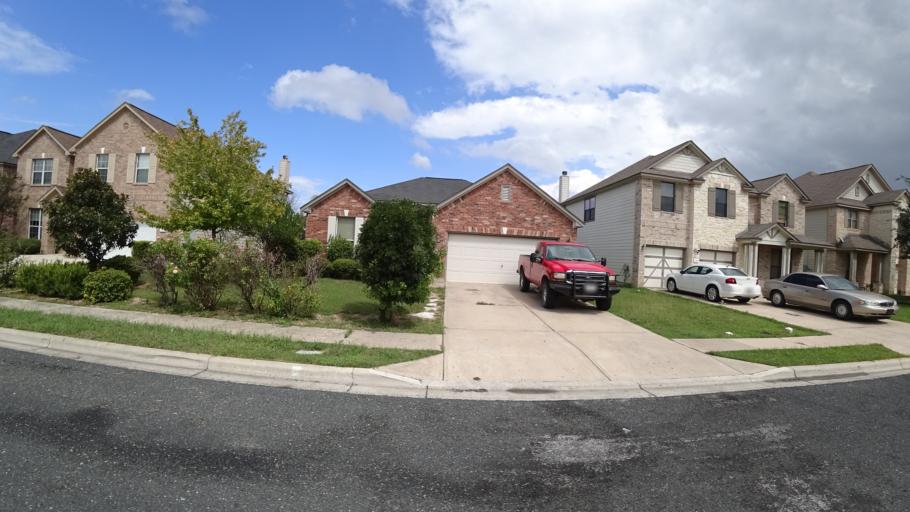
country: US
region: Texas
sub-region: Travis County
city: Onion Creek
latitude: 30.1505
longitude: -97.7479
